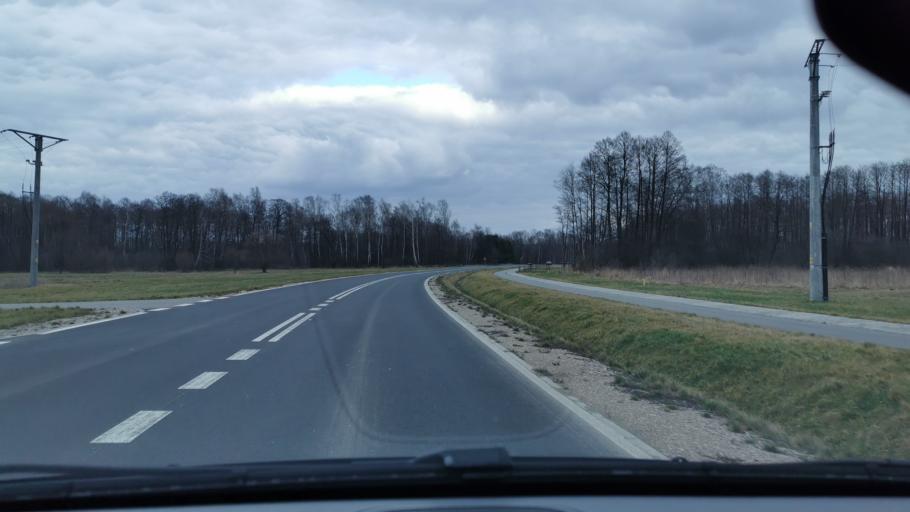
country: PL
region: Masovian Voivodeship
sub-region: Powiat zyrardowski
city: Zyrardow
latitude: 52.0070
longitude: 20.4651
